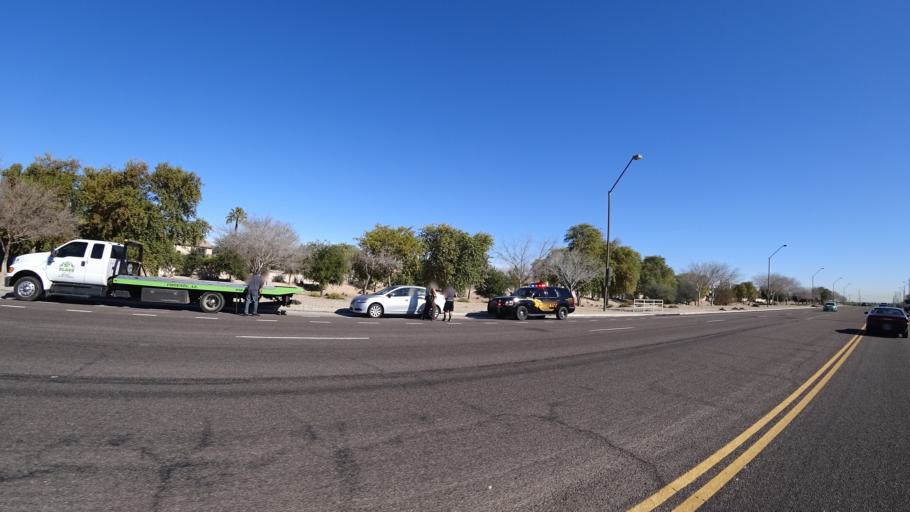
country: US
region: Arizona
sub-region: Maricopa County
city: Litchfield Park
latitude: 33.4932
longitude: -112.3315
